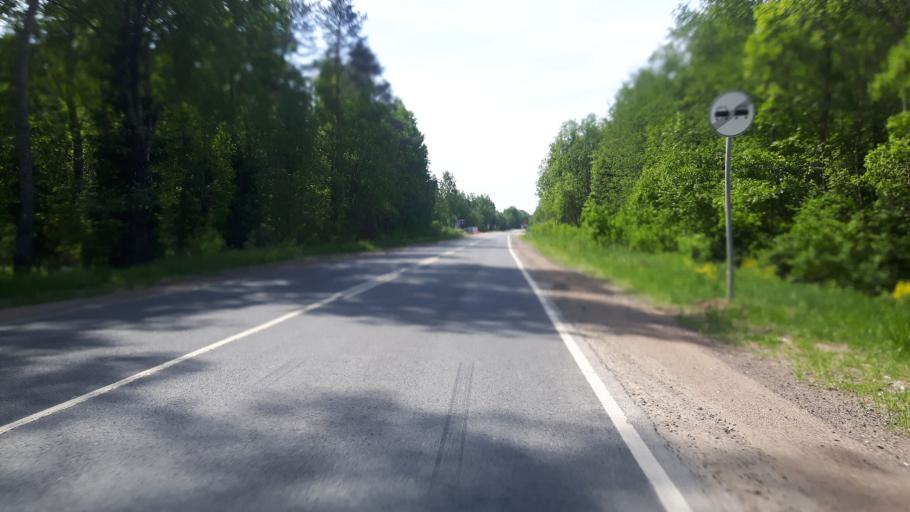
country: RU
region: Leningrad
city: Vistino
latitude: 59.6849
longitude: 28.4594
